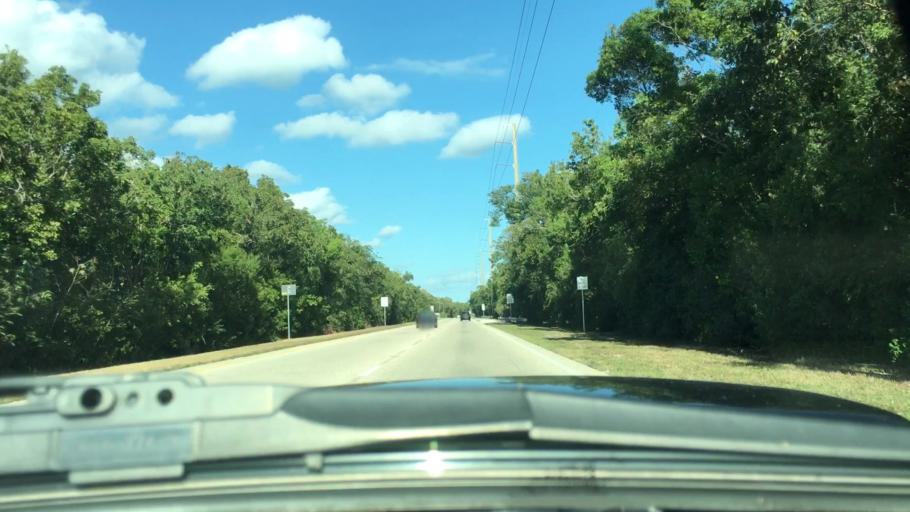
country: US
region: Florida
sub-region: Monroe County
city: Key Largo
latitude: 25.0685
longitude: -80.4680
